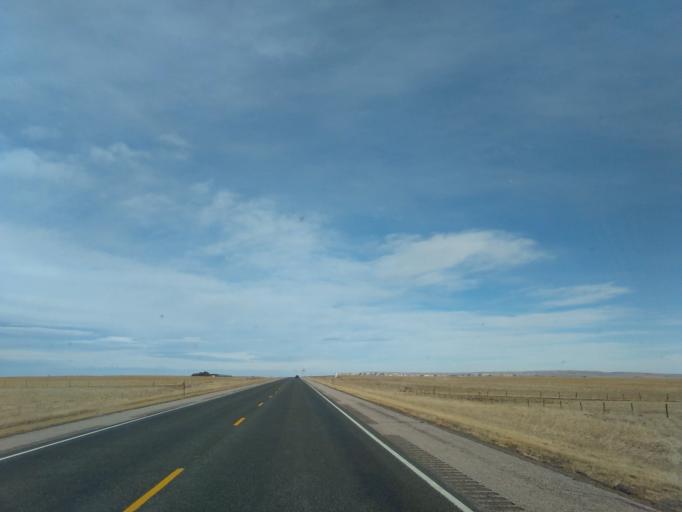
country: US
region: Wyoming
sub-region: Goshen County
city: Torrington
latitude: 41.6062
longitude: -104.2575
